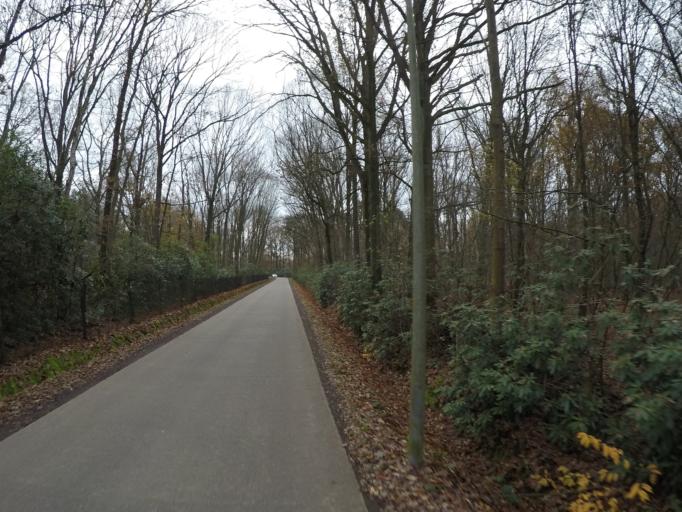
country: BE
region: Flanders
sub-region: Provincie Antwerpen
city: Heist-op-den-Berg
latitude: 51.1043
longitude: 4.7081
